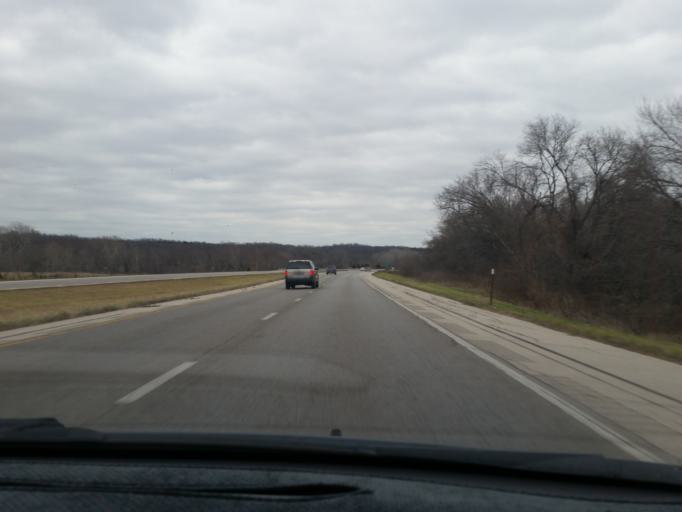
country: US
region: Kansas
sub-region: Johnson County
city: De Soto
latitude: 38.9572
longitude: -94.9192
